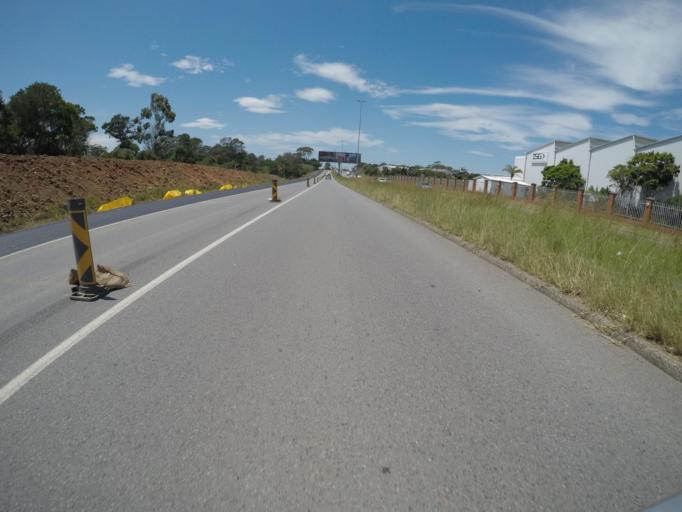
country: ZA
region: Eastern Cape
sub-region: Buffalo City Metropolitan Municipality
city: East London
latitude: -33.0360
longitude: 27.8373
